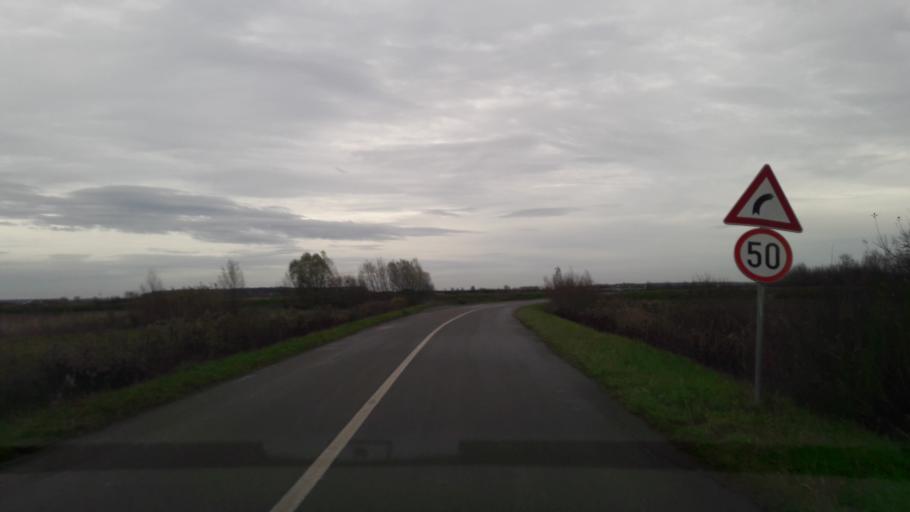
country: HR
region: Virovitick-Podravska
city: Zdenci
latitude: 45.6098
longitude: 18.0220
